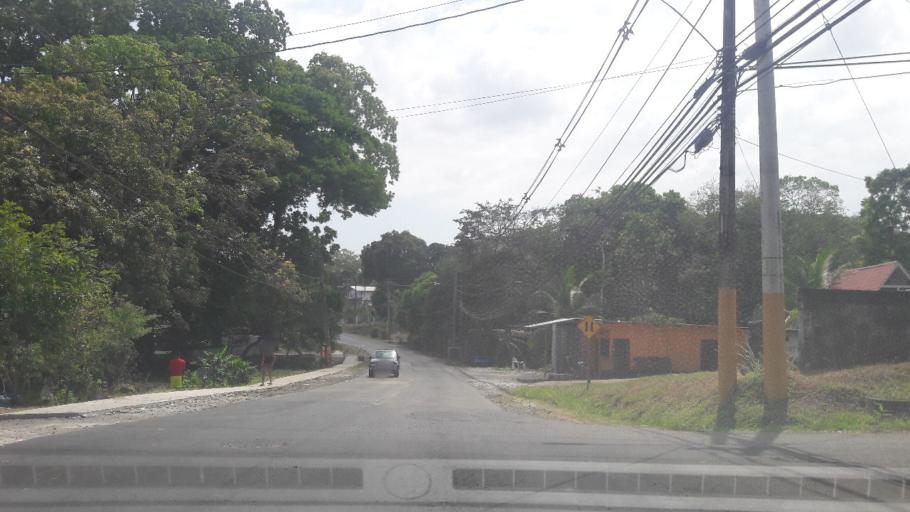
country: PA
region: Panama
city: La Cabima
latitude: 9.1210
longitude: -79.5448
